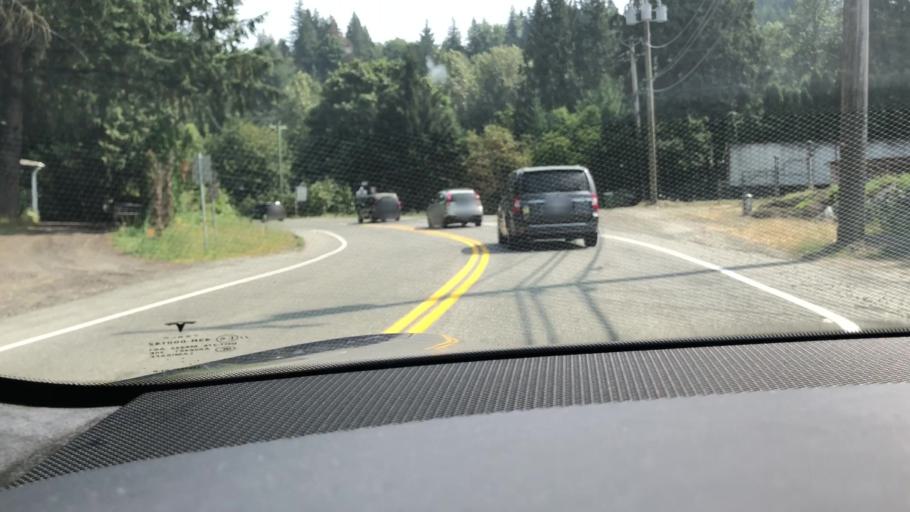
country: CA
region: British Columbia
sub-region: Fraser Valley Regional District
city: Chilliwack
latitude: 49.0935
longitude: -121.9722
